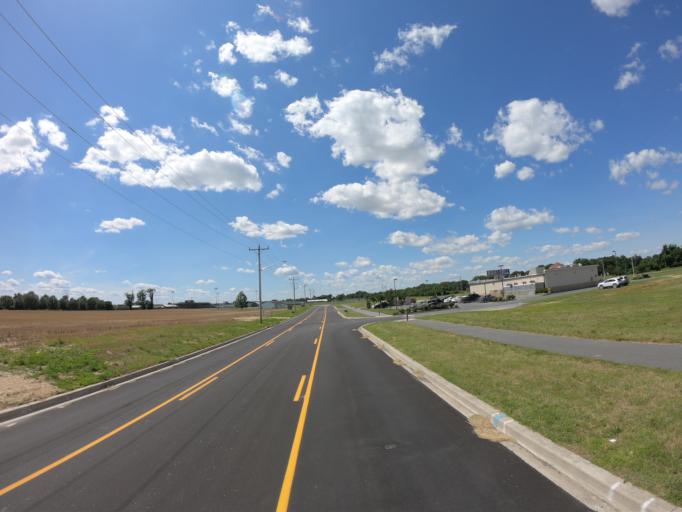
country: US
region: Delaware
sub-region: Sussex County
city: Milford
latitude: 38.9283
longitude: -75.4194
